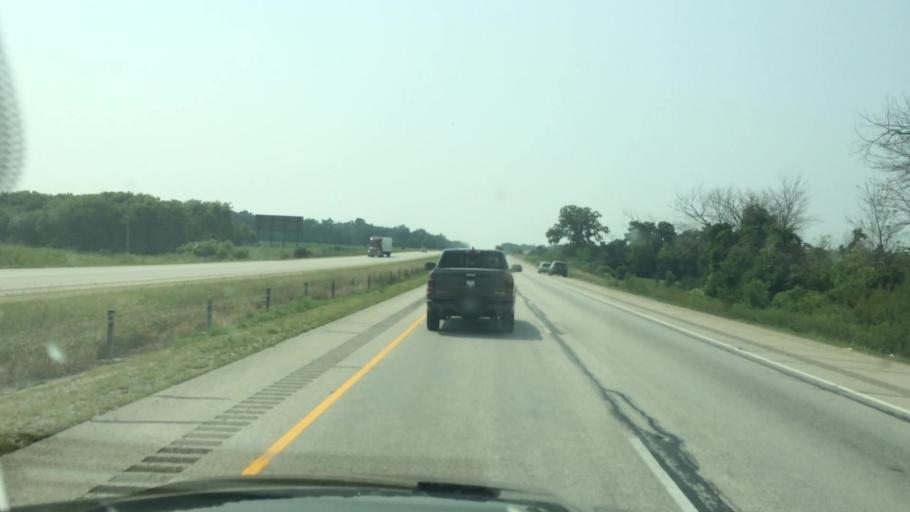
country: US
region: Wisconsin
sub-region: Fond du Lac County
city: Fond du Lac
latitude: 43.7210
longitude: -88.4426
